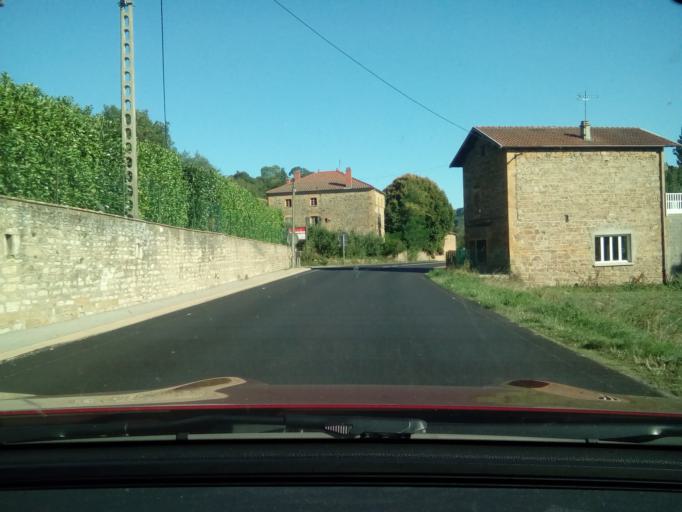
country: FR
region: Rhone-Alpes
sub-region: Departement du Rhone
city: Chatillon
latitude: 45.8956
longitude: 4.5944
